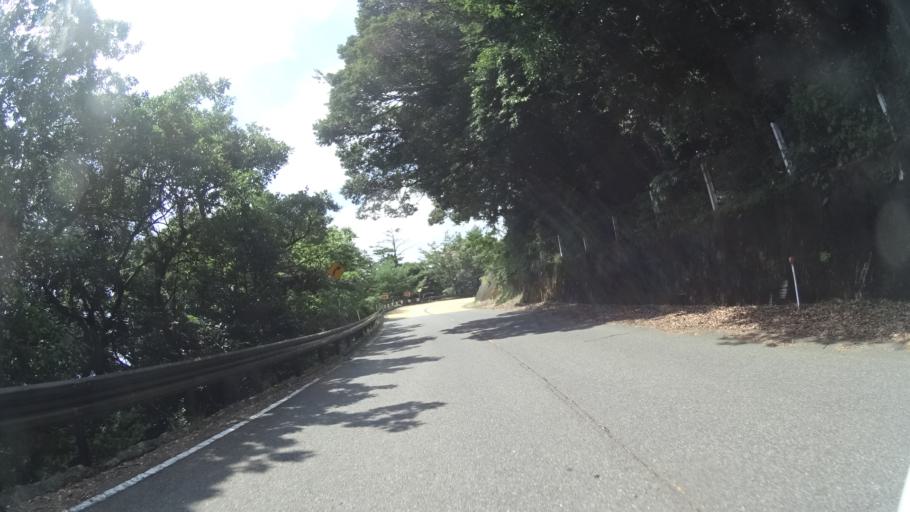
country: JP
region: Miyazaki
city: Kobayashi
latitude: 31.9013
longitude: 130.8401
